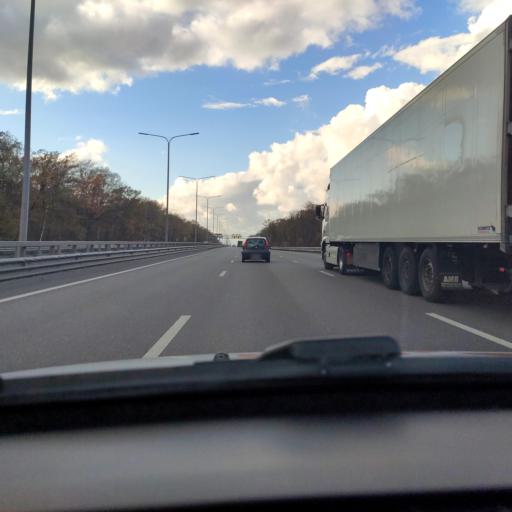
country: RU
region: Voronezj
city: Podgornoye
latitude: 51.8322
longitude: 39.2361
